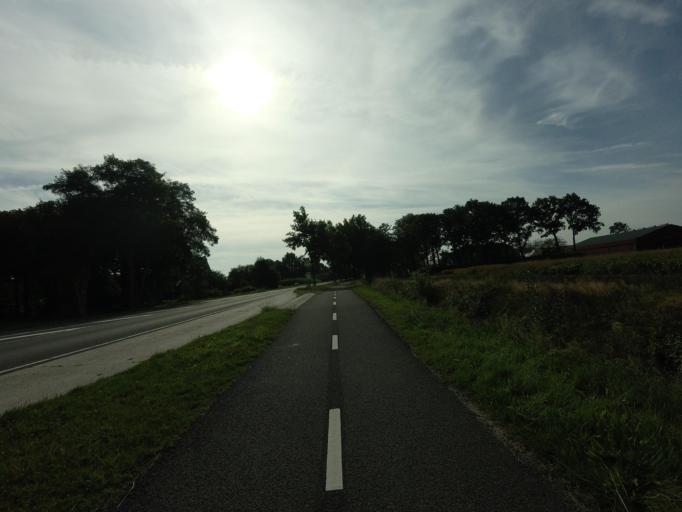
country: NL
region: Drenthe
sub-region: Gemeente Aa en Hunze
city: Anloo
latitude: 52.9666
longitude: 6.6569
